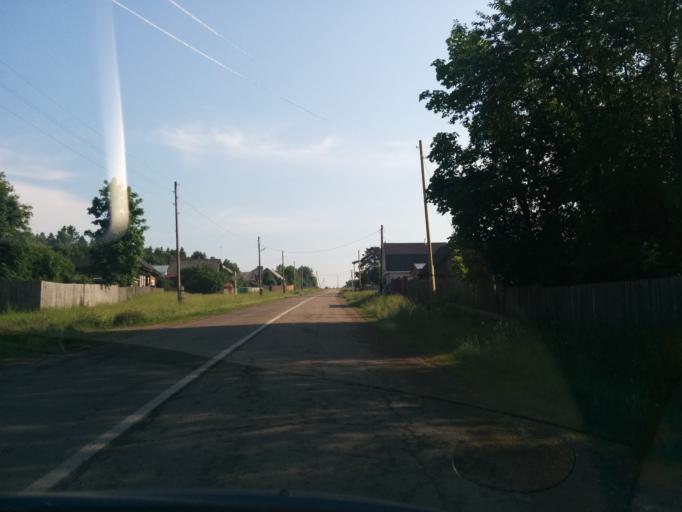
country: RU
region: Perm
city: Polazna
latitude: 58.2456
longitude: 56.2683
